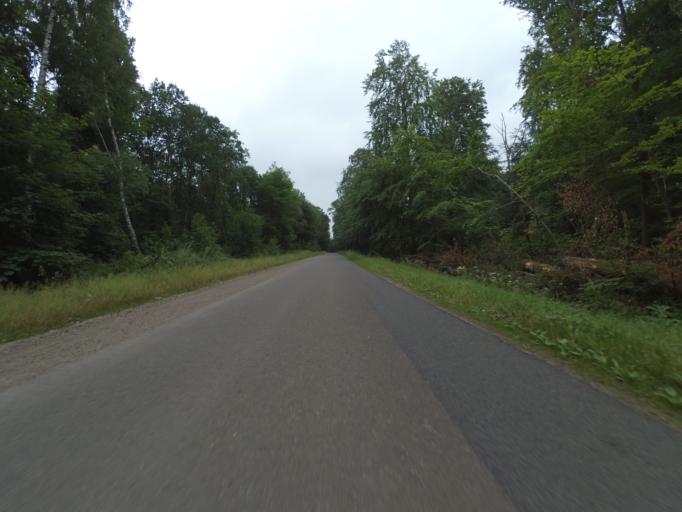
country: DE
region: Mecklenburg-Vorpommern
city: Spornitz
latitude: 53.3612
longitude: 11.6995
